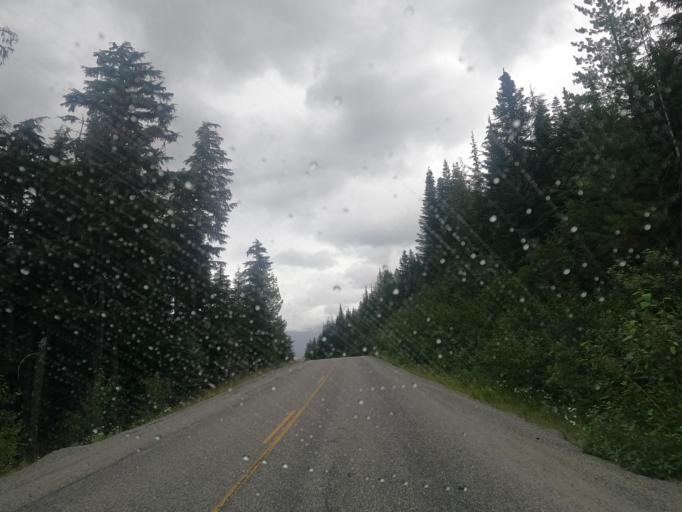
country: CA
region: British Columbia
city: Pemberton
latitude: 50.3918
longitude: -122.3381
